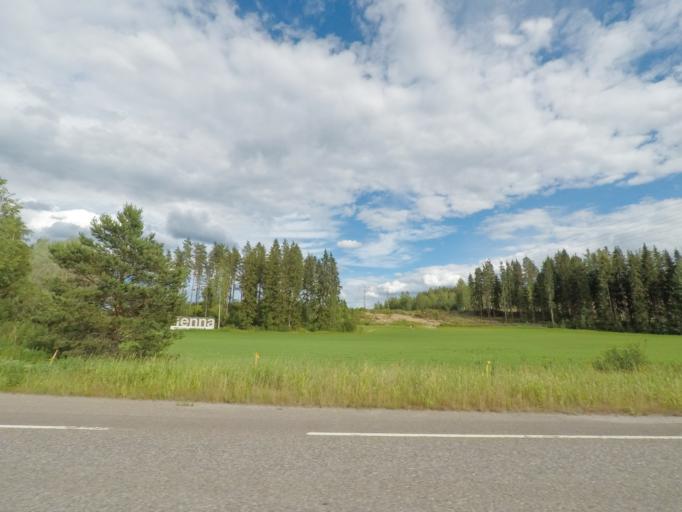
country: FI
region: Uusimaa
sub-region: Porvoo
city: Pukkila
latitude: 60.8010
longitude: 25.4740
